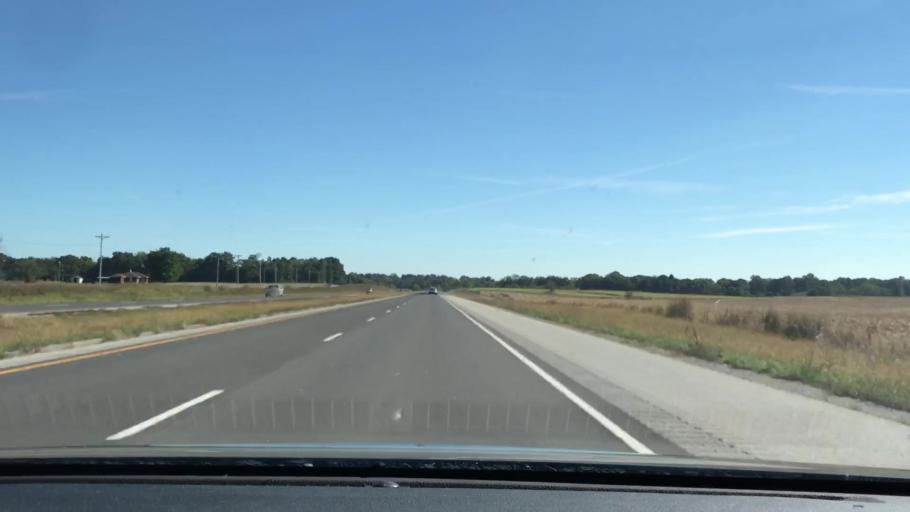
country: US
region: Kentucky
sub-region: Todd County
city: Elkton
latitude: 36.8133
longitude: -87.0233
